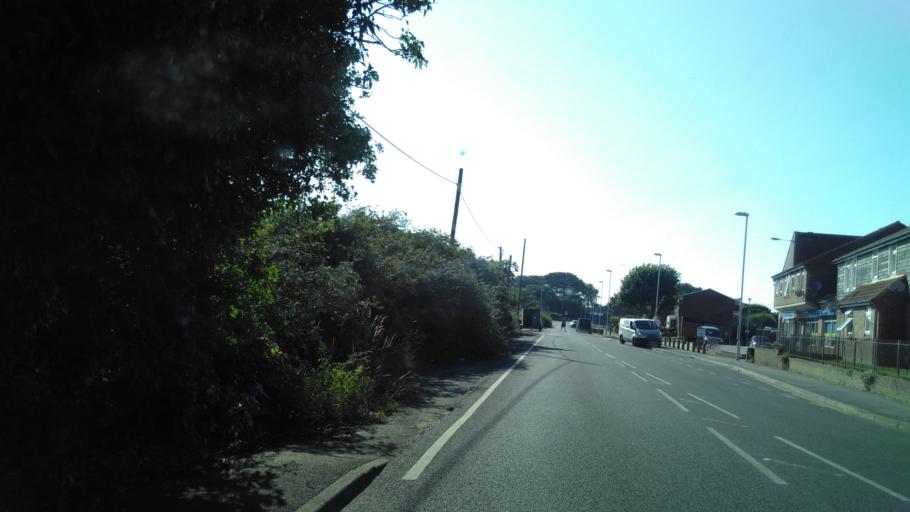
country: GB
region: England
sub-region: Kent
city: Whitstable
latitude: 51.3432
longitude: 0.9957
